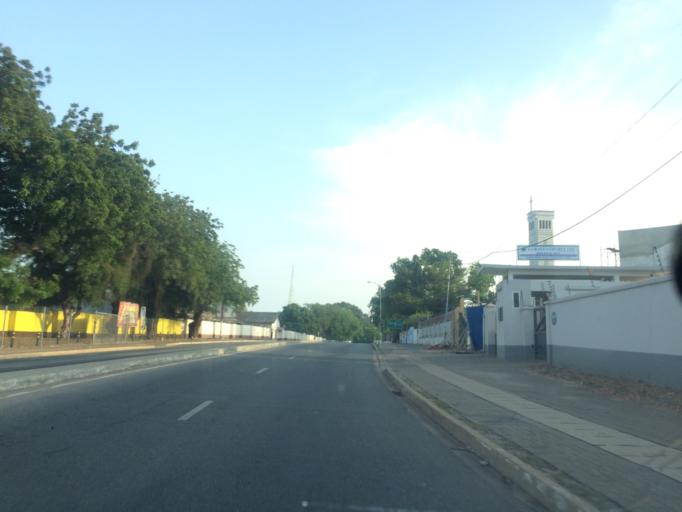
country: GH
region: Greater Accra
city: Accra
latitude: 5.5643
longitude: -0.2064
